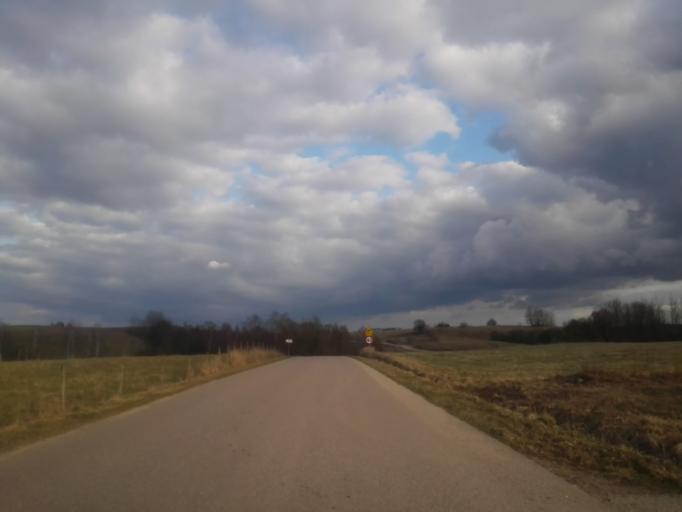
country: PL
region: Podlasie
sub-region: Suwalki
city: Suwalki
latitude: 54.2062
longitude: 22.9807
